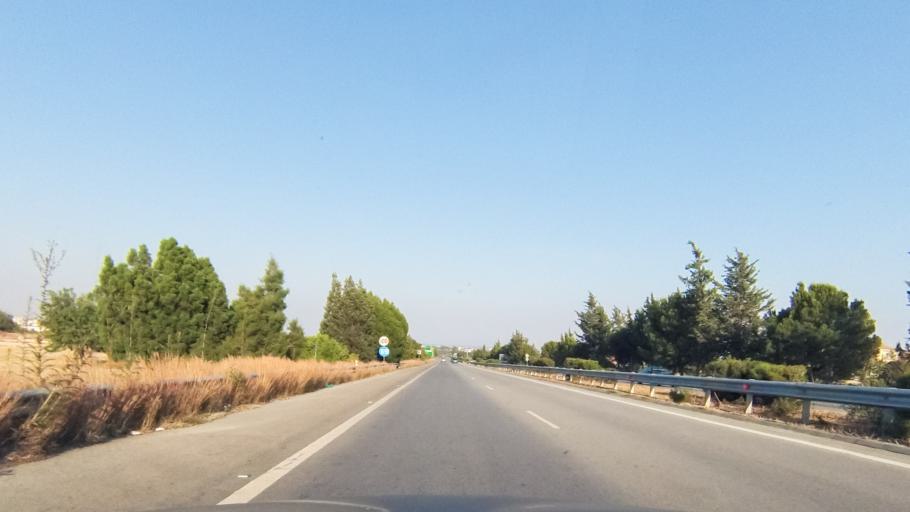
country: CY
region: Limassol
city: Ypsonas
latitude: 34.6929
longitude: 32.9734
